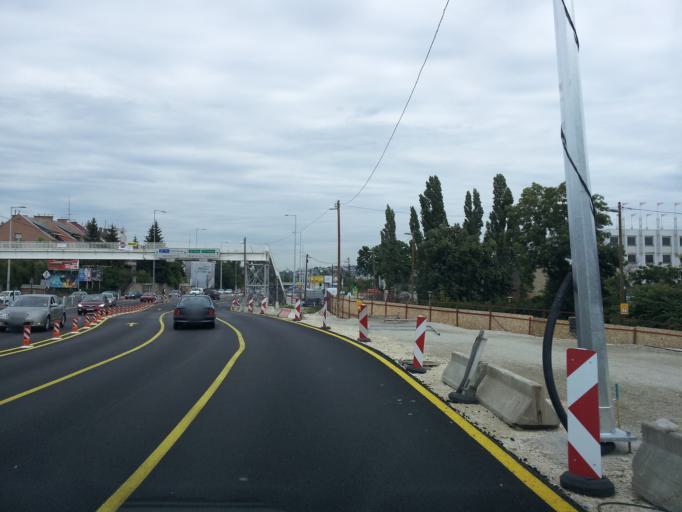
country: HU
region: Budapest
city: Budapest XI. keruelet
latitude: 47.4667
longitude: 19.0168
